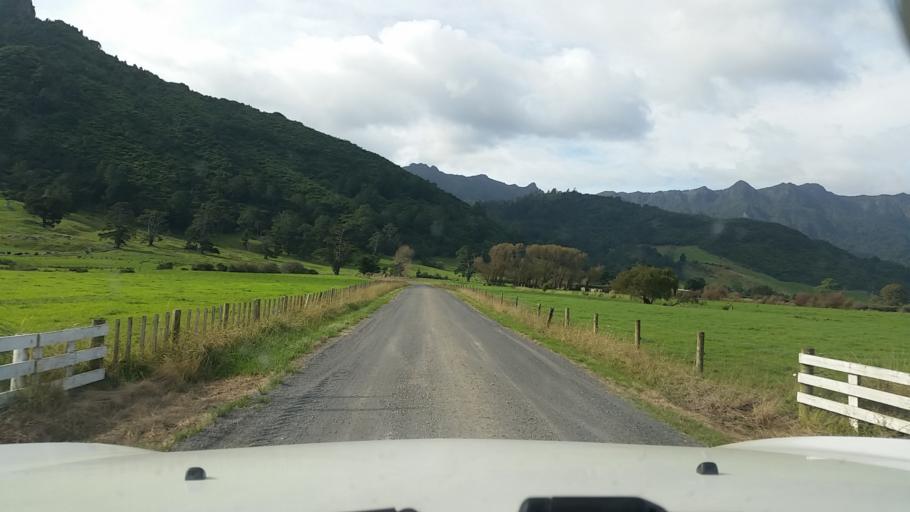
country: NZ
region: Bay of Plenty
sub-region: Western Bay of Plenty District
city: Katikati
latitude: -37.5640
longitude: 175.7416
